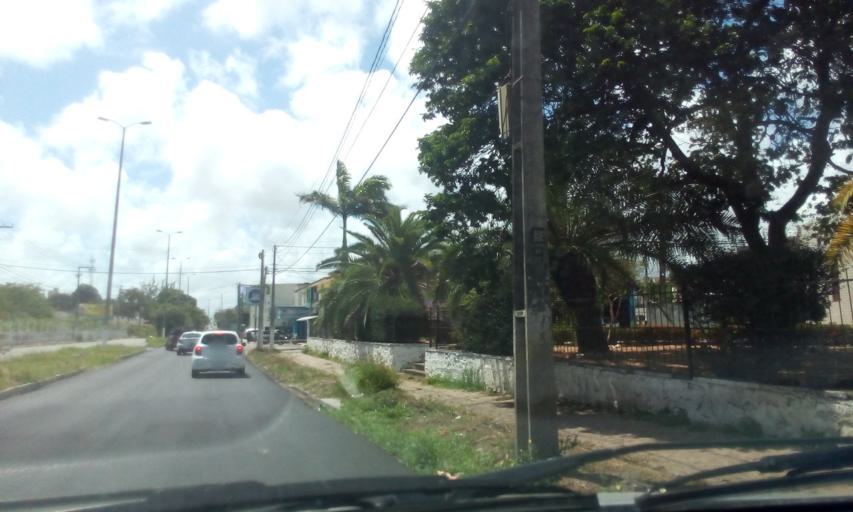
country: BR
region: Rio Grande do Norte
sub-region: Natal
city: Natal
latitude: -5.8637
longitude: -35.2050
